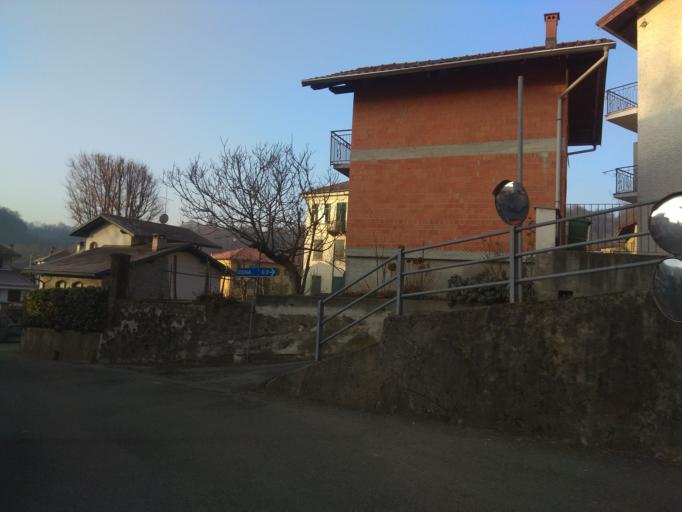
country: IT
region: Piedmont
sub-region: Provincia di Biella
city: Pray
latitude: 45.6760
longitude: 8.2044
